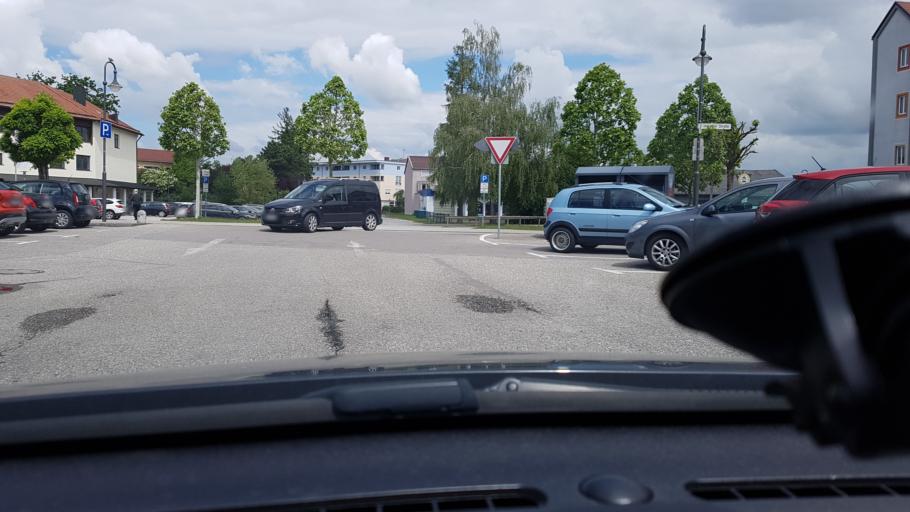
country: DE
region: Bavaria
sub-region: Lower Bavaria
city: Pocking
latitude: 48.4012
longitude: 13.3136
